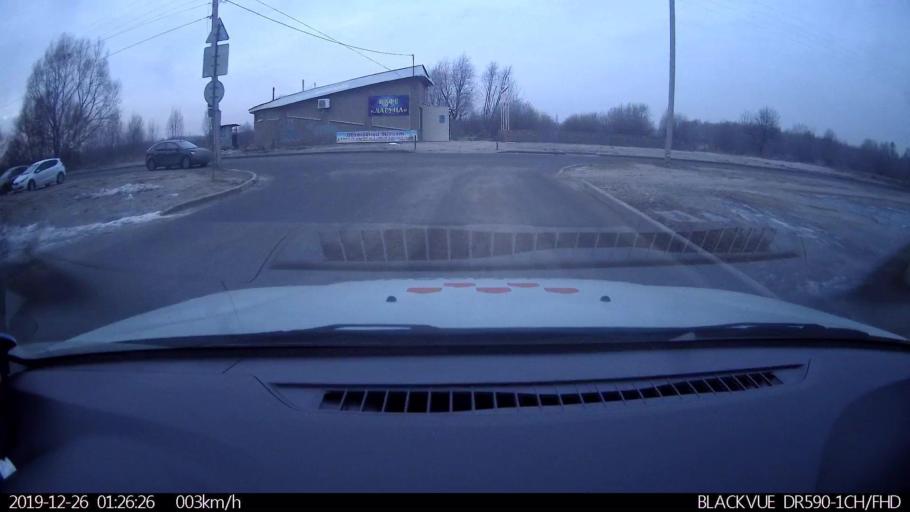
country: RU
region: Nizjnij Novgorod
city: Gorbatovka
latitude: 56.2668
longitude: 43.8651
